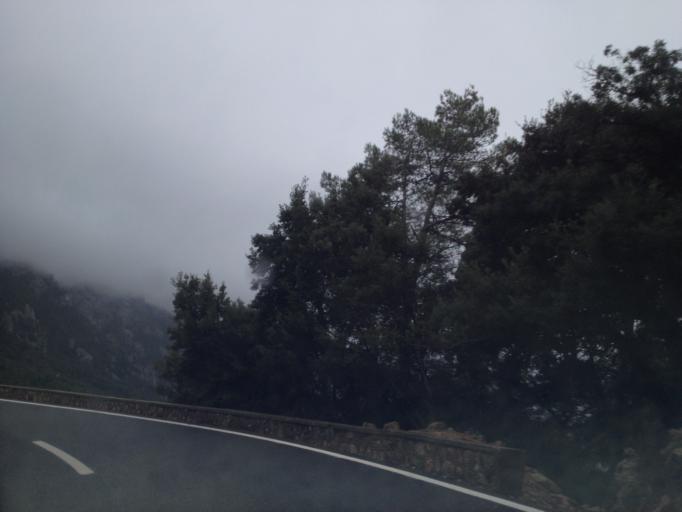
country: ES
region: Balearic Islands
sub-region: Illes Balears
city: Fornalutx
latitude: 39.7984
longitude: 2.7730
